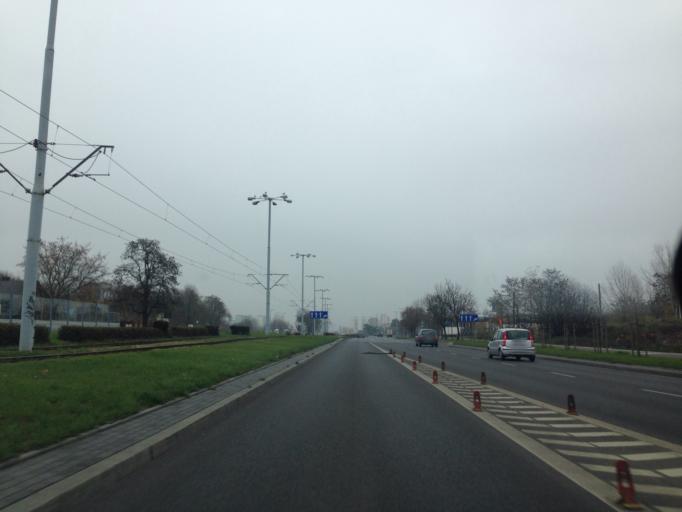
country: PL
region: Kujawsko-Pomorskie
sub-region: Torun
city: Torun
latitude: 53.0220
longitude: 18.6526
